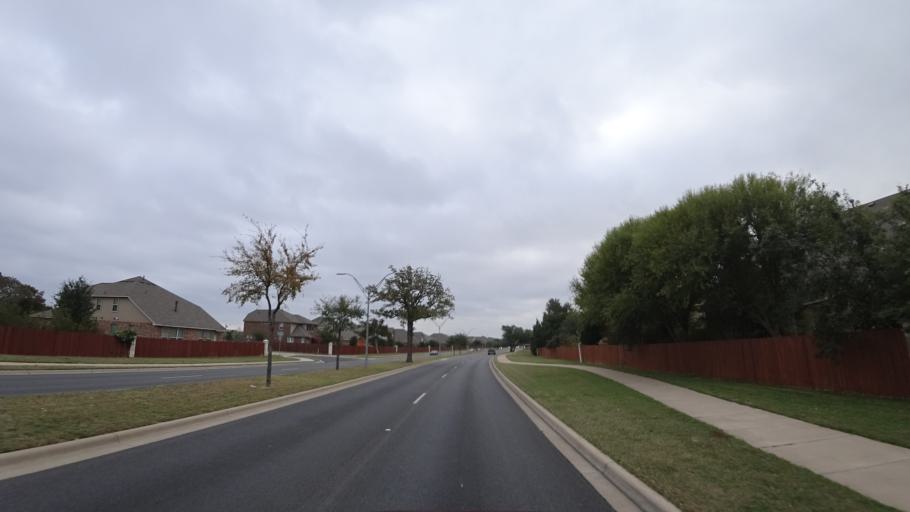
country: US
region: Texas
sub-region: Williamson County
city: Cedar Park
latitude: 30.4970
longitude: -97.8433
